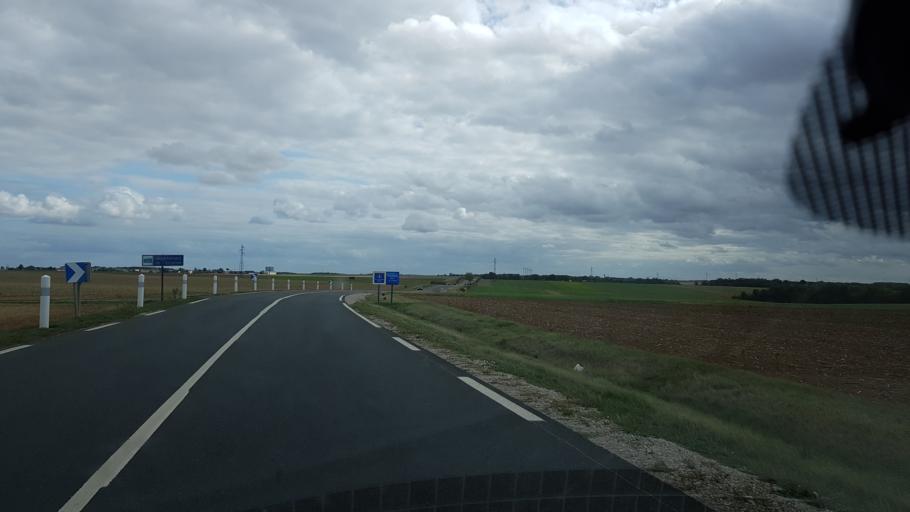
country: FR
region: Centre
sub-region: Departement du Loiret
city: Sermaises
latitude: 48.3282
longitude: 2.1962
